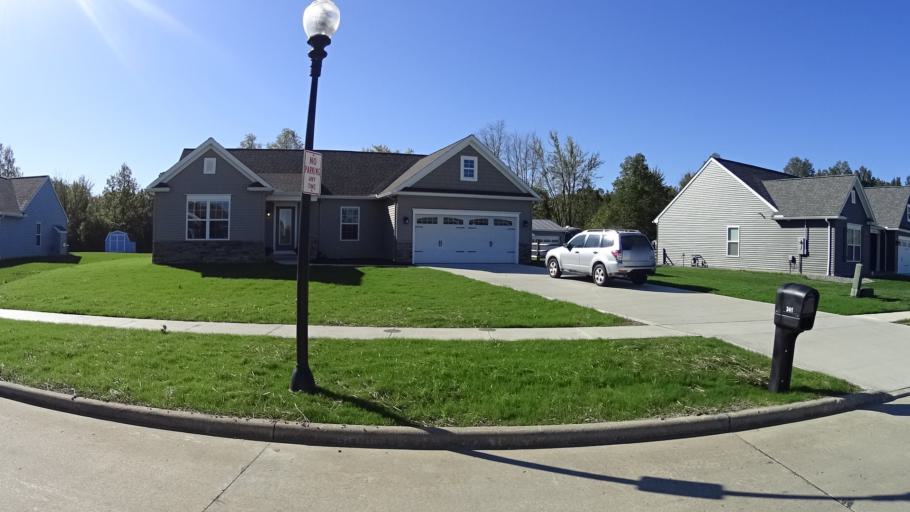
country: US
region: Ohio
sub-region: Lorain County
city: Oberlin
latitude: 41.2740
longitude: -82.2291
